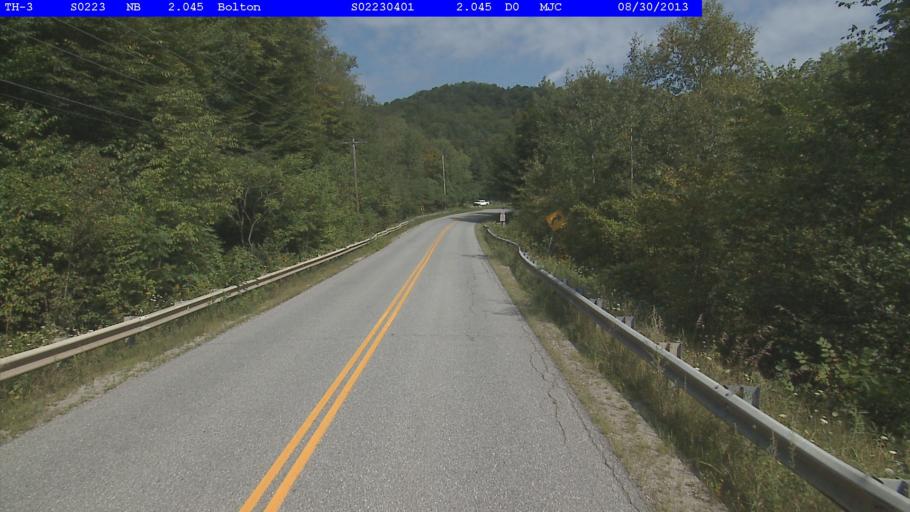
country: US
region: Vermont
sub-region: Washington County
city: Waterbury
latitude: 44.3990
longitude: -72.8788
